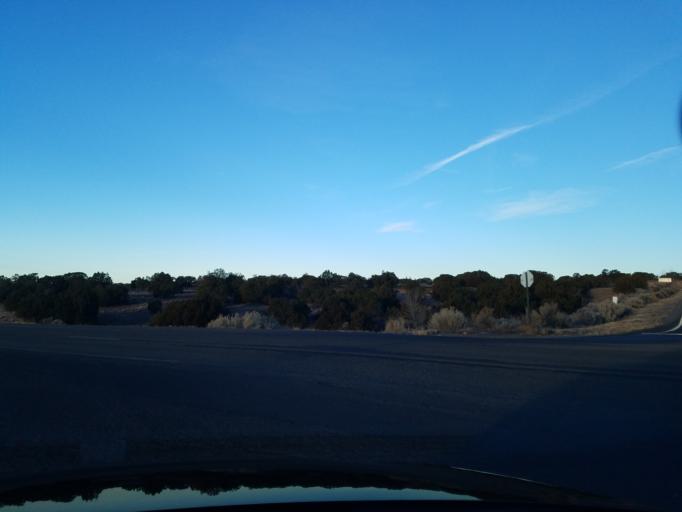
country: US
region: New Mexico
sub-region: Santa Fe County
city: Agua Fria
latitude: 35.6765
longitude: -106.0128
